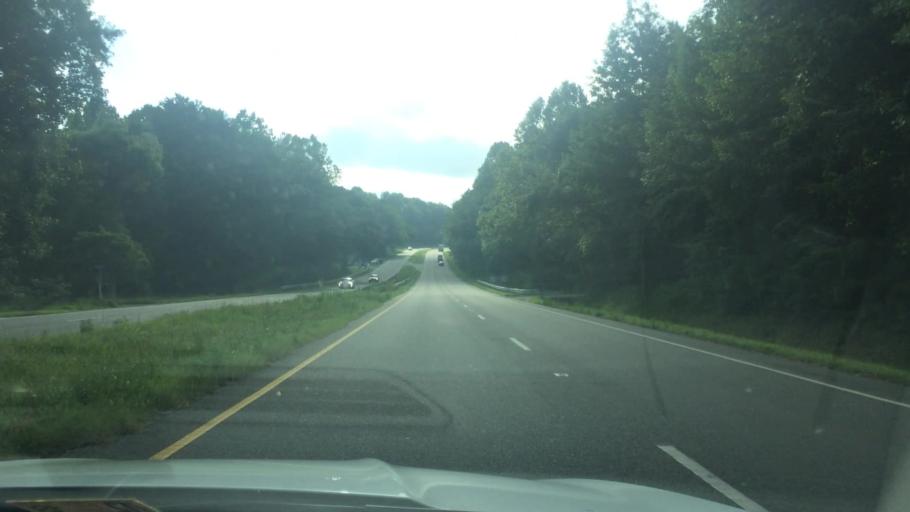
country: US
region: Virginia
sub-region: Gloucester County
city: Gloucester Courthouse
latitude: 37.4261
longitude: -76.4978
